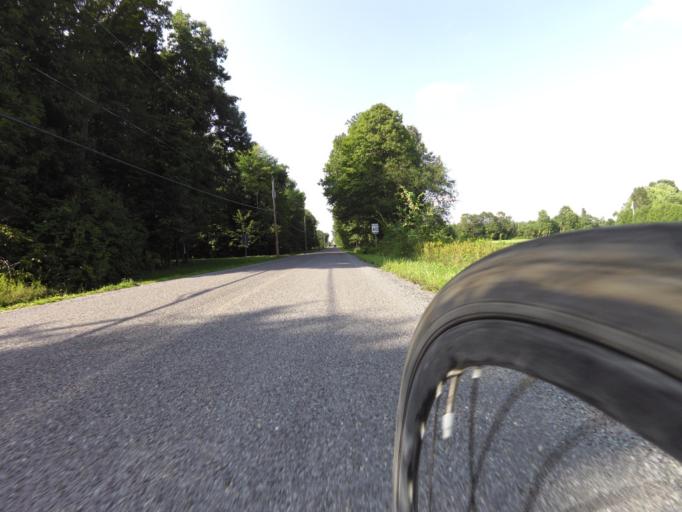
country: CA
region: Ontario
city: Kingston
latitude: 44.3753
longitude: -76.5951
